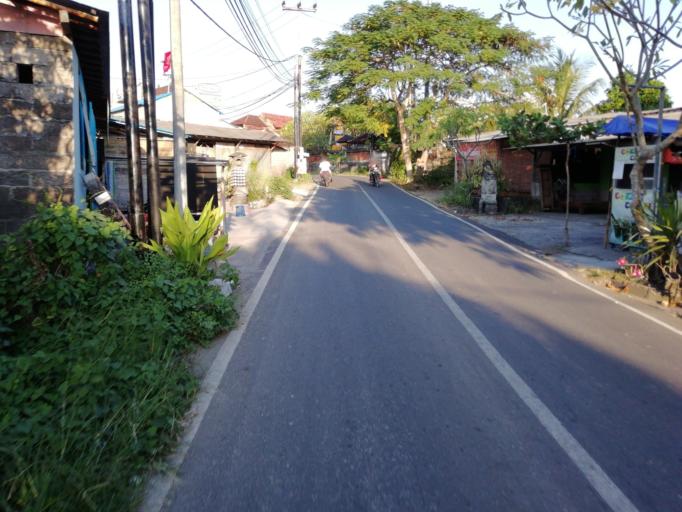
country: ID
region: Bali
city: Bualu
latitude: -8.7967
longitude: 115.1934
